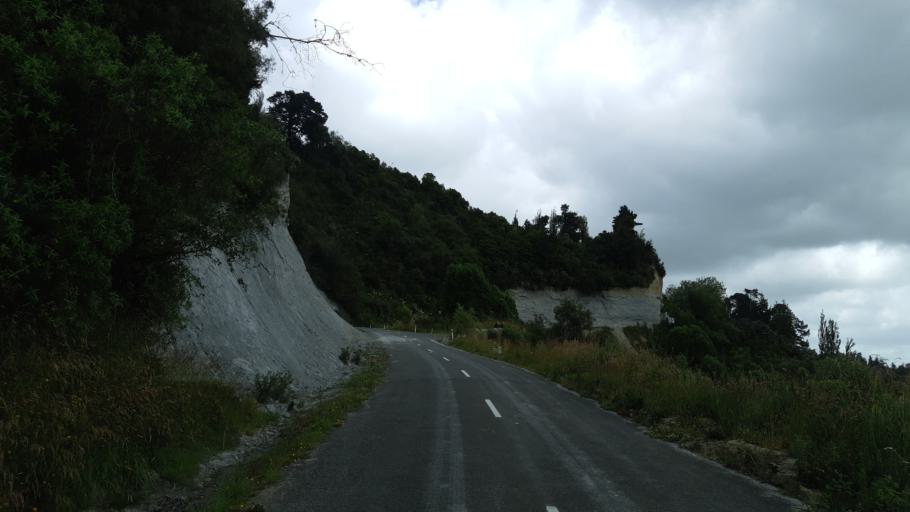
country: NZ
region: Manawatu-Wanganui
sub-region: Ruapehu District
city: Waiouru
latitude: -39.9221
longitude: 175.9437
